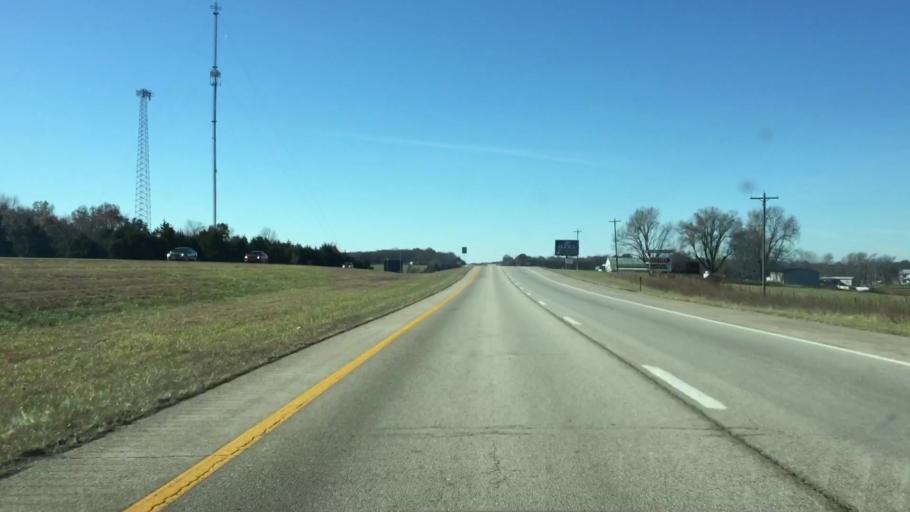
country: US
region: Missouri
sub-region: Cole County
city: Saint Martins
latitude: 38.4154
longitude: -92.3459
